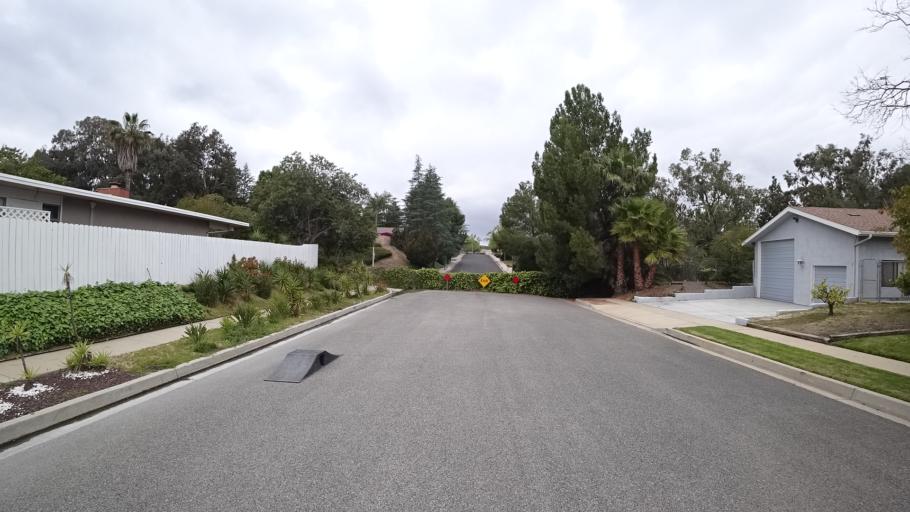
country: US
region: California
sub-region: Ventura County
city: Casa Conejo
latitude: 34.2035
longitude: -118.8893
